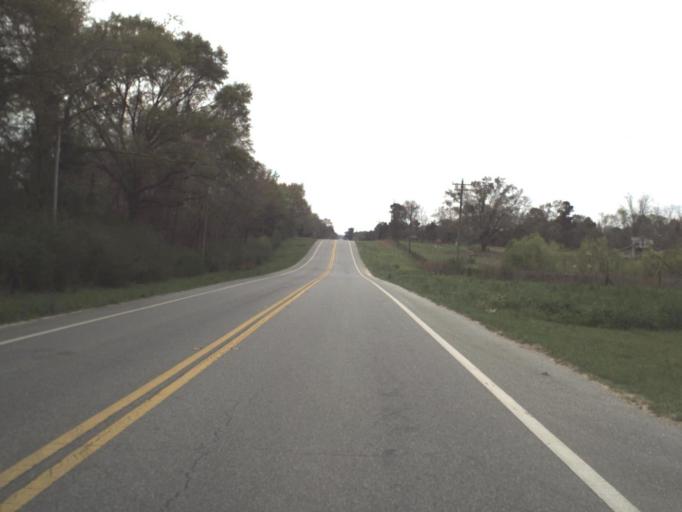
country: US
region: Florida
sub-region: Jackson County
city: Graceville
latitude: 30.9509
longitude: -85.6490
